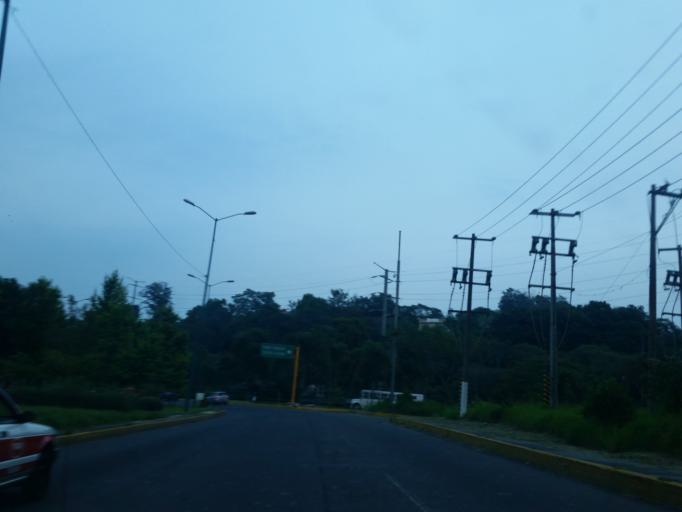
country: MX
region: Veracruz
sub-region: Xalapa
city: Xalapa de Enriquez
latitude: 19.5083
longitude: -96.9295
